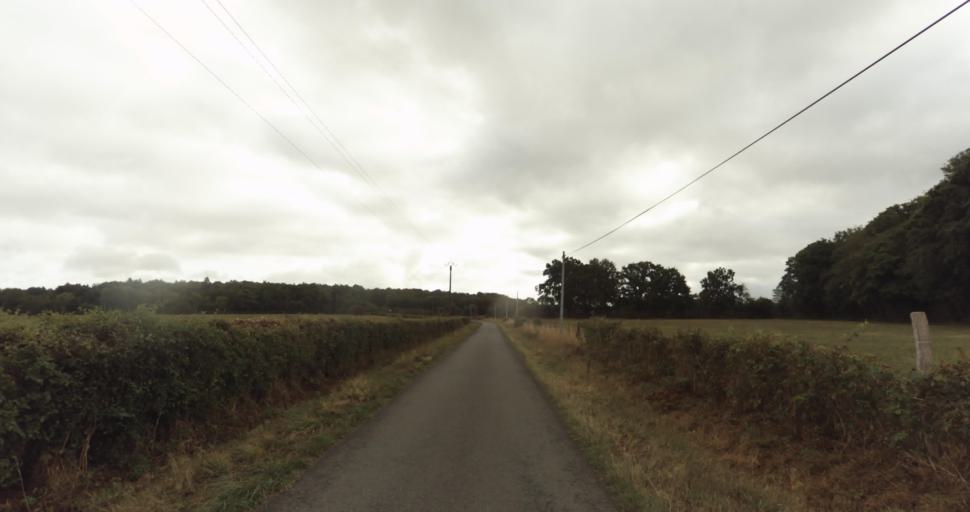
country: FR
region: Lower Normandy
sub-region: Departement de l'Orne
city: Gace
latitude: 48.8716
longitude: 0.3003
